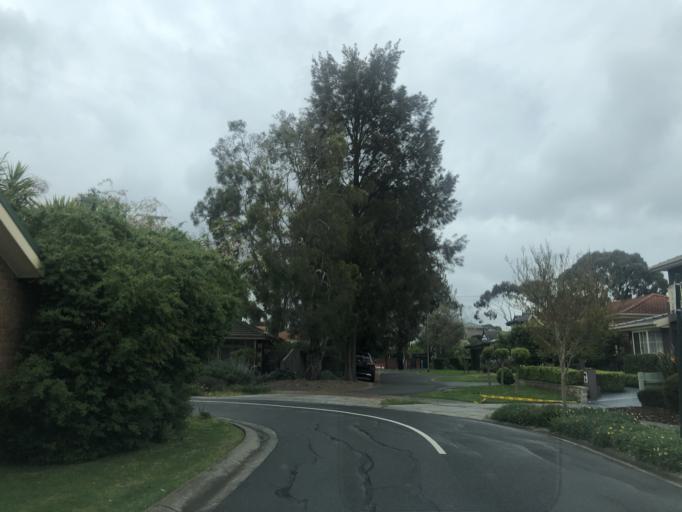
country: AU
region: Victoria
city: Burwood East
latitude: -37.8576
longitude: 145.1395
